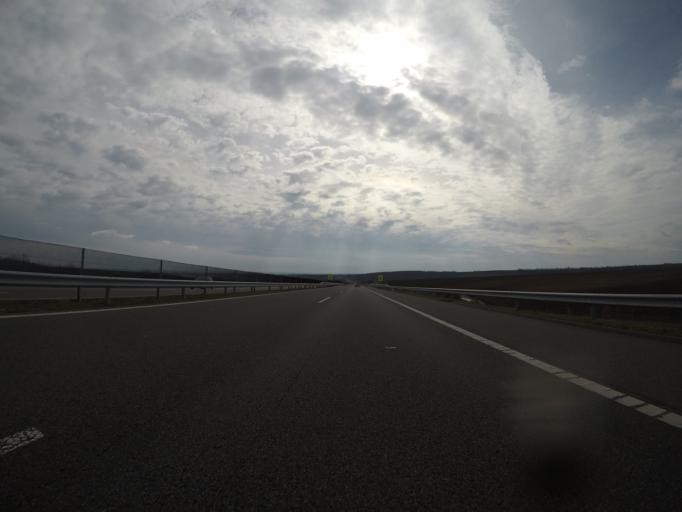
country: HU
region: Baranya
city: Lanycsok
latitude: 46.0313
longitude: 18.5724
